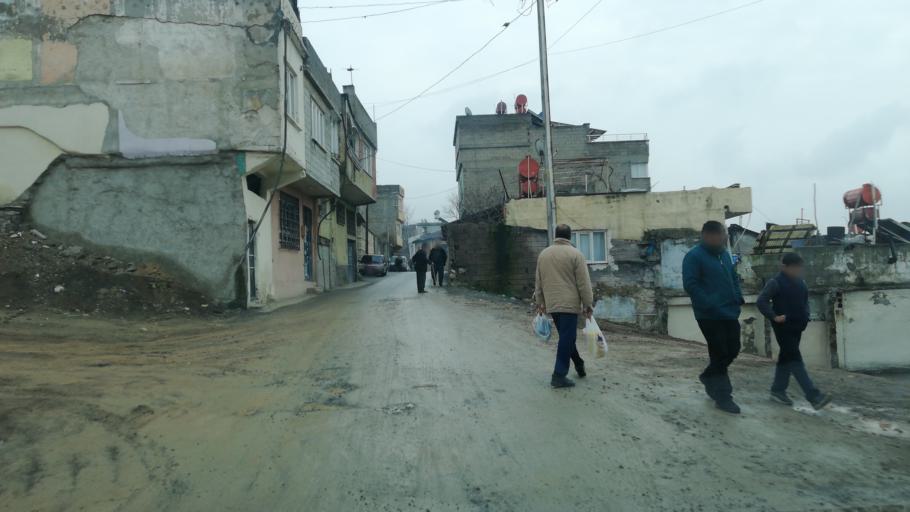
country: TR
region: Kahramanmaras
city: Kahramanmaras
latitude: 37.5817
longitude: 36.9336
